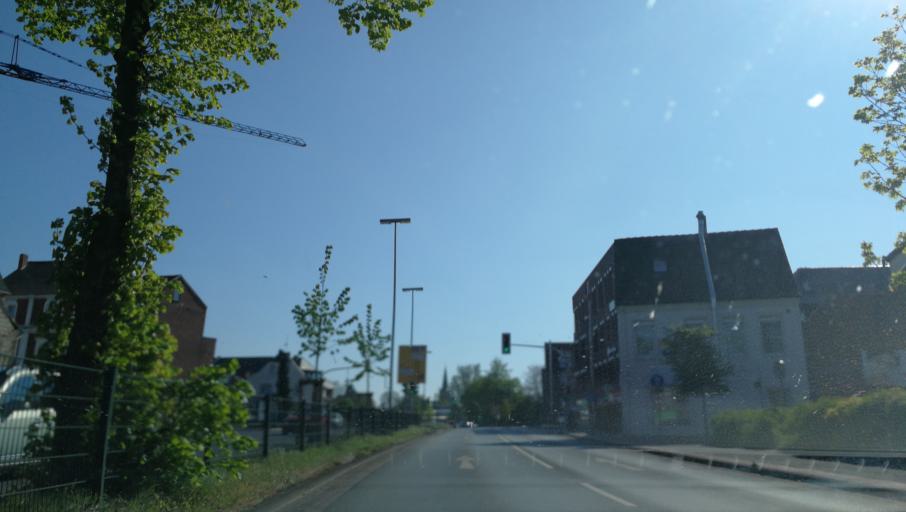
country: DE
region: North Rhine-Westphalia
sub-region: Regierungsbezirk Munster
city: Rheine
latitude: 52.2801
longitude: 7.4456
